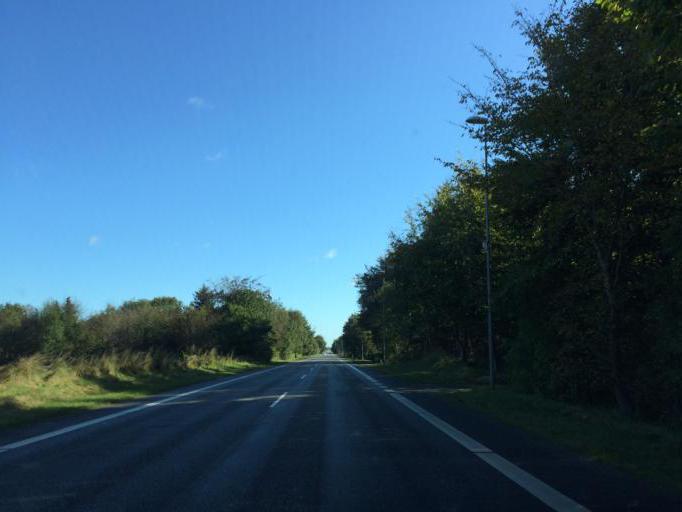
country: DK
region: Central Jutland
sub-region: Holstebro Kommune
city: Vinderup
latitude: 56.4021
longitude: 8.9503
